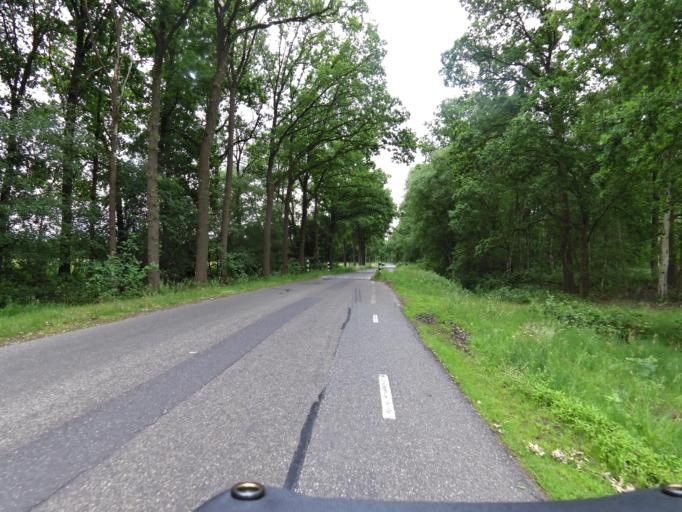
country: NL
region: North Brabant
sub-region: Gemeente Oirschot
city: Middelbeers
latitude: 51.4313
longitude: 5.2120
